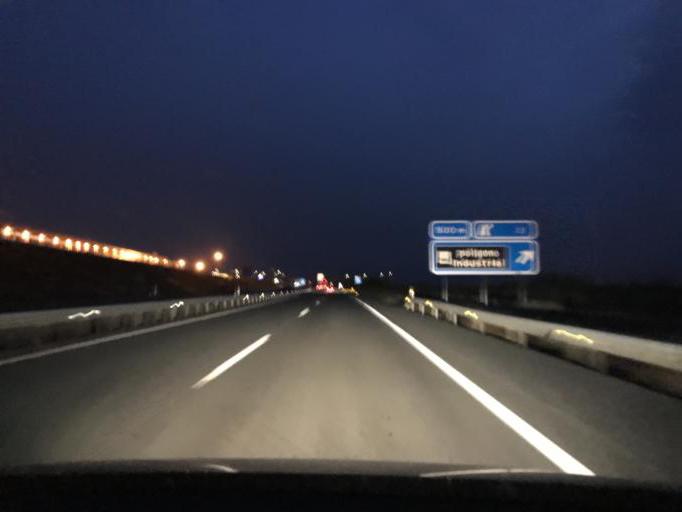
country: ES
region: Andalusia
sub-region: Provincia de Granada
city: Guadix
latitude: 37.3444
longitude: -3.0920
